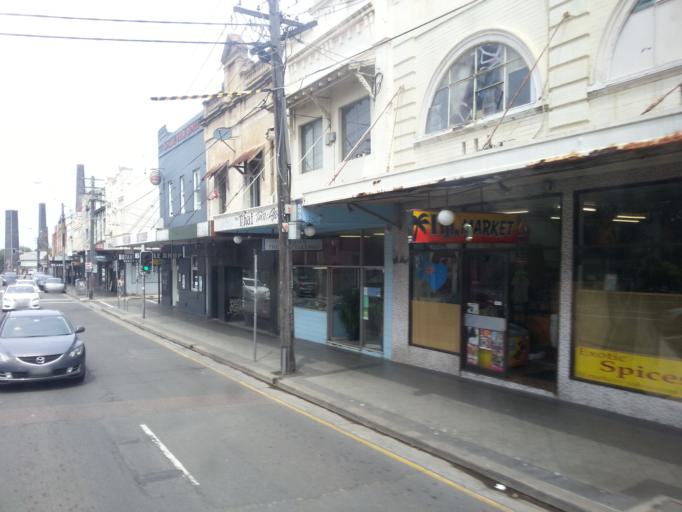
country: AU
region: New South Wales
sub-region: Marrickville
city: Newtown
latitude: -33.9057
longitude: 151.1809
